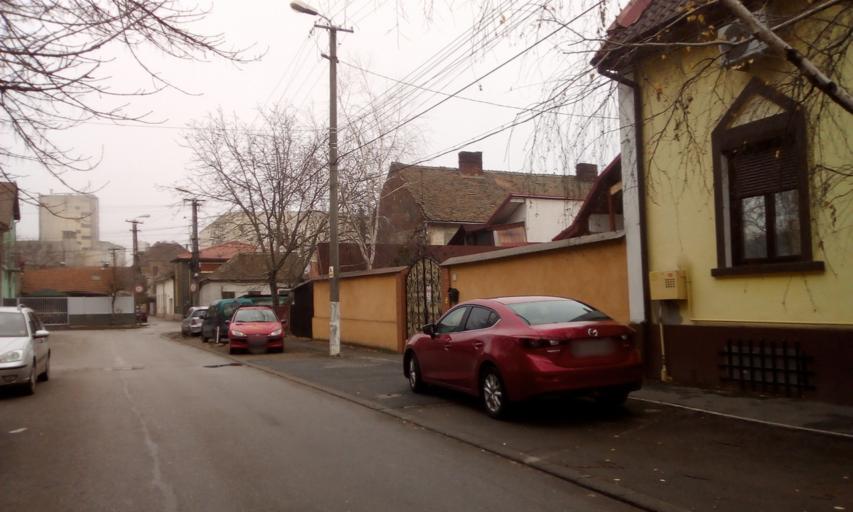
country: RO
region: Timis
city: Timisoara
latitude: 45.7497
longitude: 21.2482
